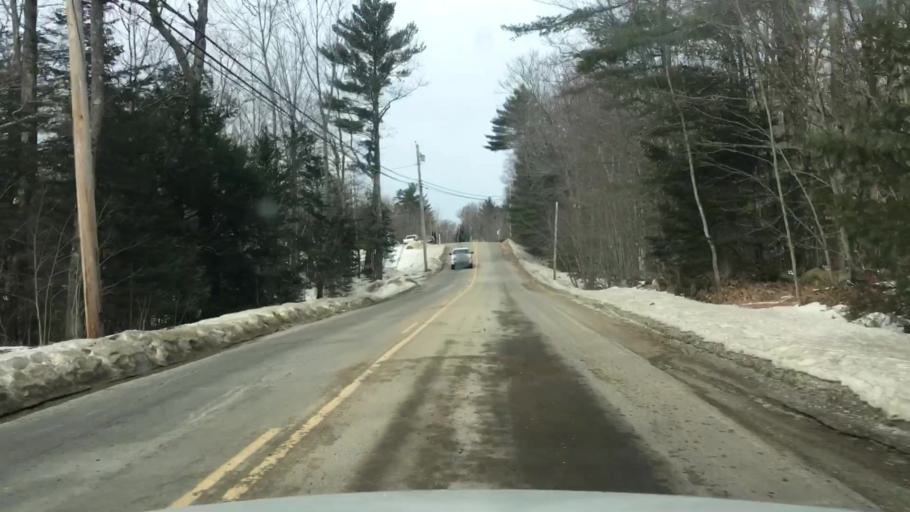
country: US
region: Maine
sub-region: Kennebec County
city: Chelsea
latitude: 44.2529
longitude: -69.6390
